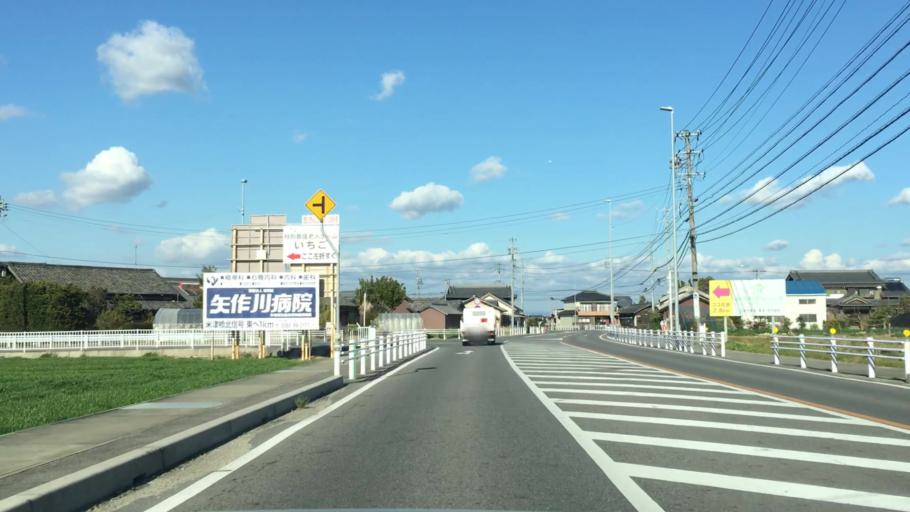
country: JP
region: Aichi
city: Ishiki
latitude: 34.8292
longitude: 137.0388
